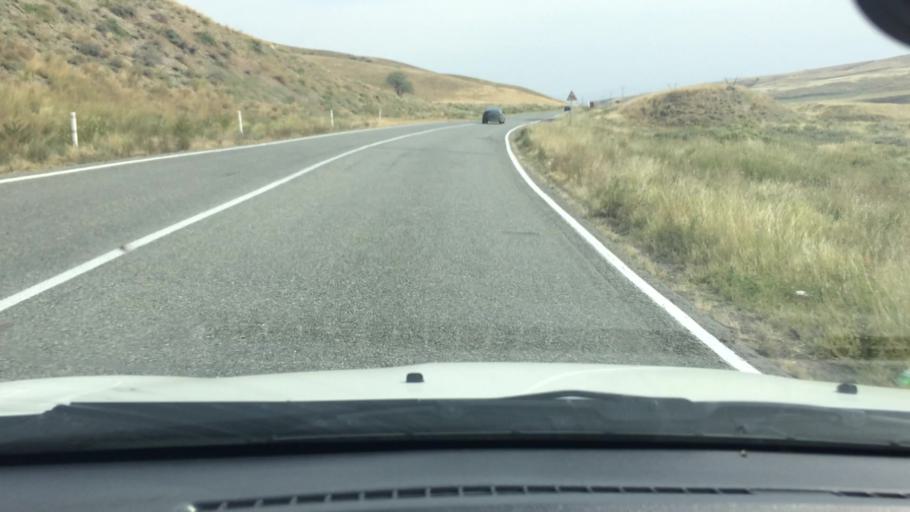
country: GE
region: Kvemo Kartli
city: Rust'avi
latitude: 41.5062
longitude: 44.9528
